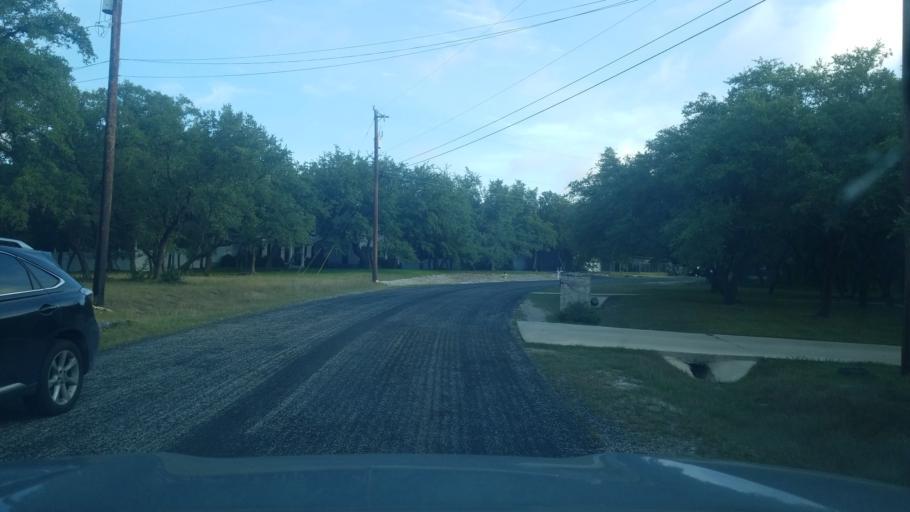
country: US
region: Texas
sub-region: Bexar County
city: Timberwood Park
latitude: 29.7005
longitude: -98.5092
